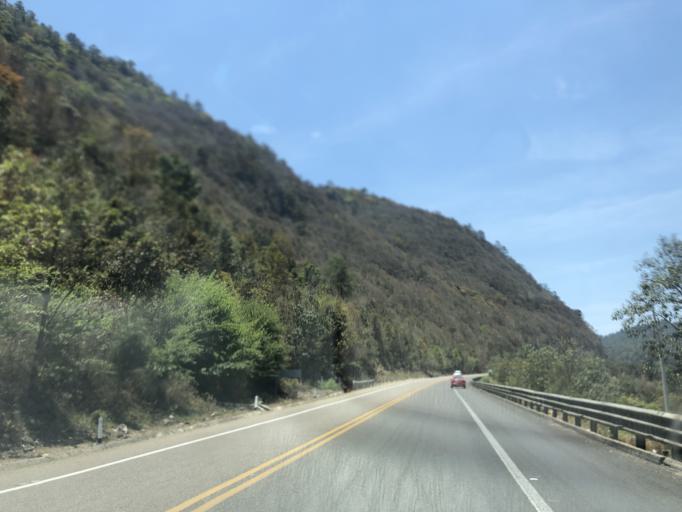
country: MX
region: Chiapas
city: San Cristobal de las Casas
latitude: 16.7195
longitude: -92.6663
